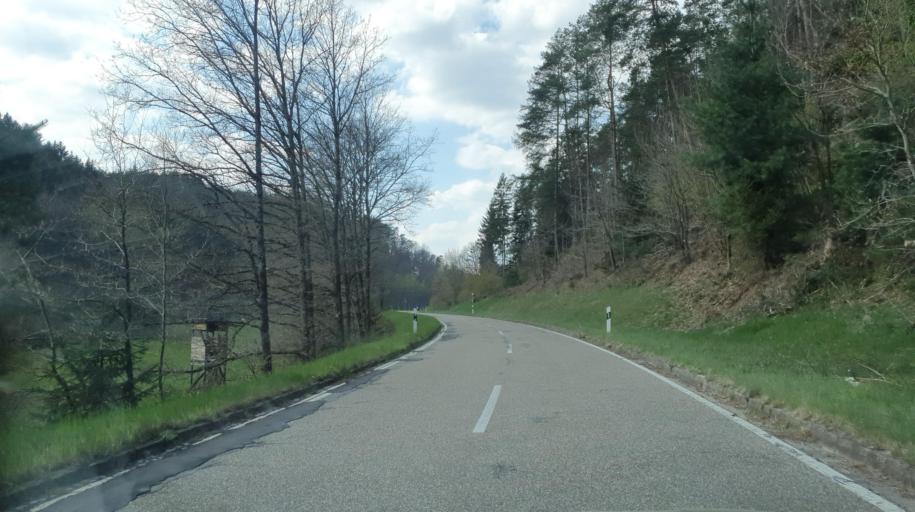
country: DE
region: Rheinland-Pfalz
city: Clausen
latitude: 49.2703
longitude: 7.6824
